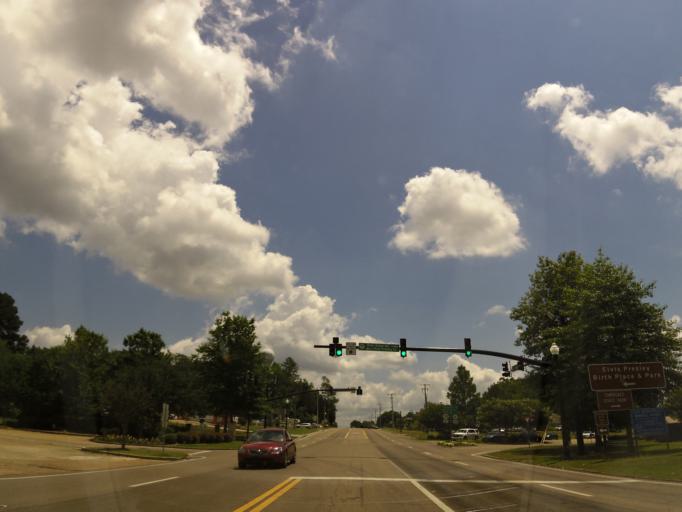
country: US
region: Mississippi
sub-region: Lee County
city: Tupelo
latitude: 34.2576
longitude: -88.6807
